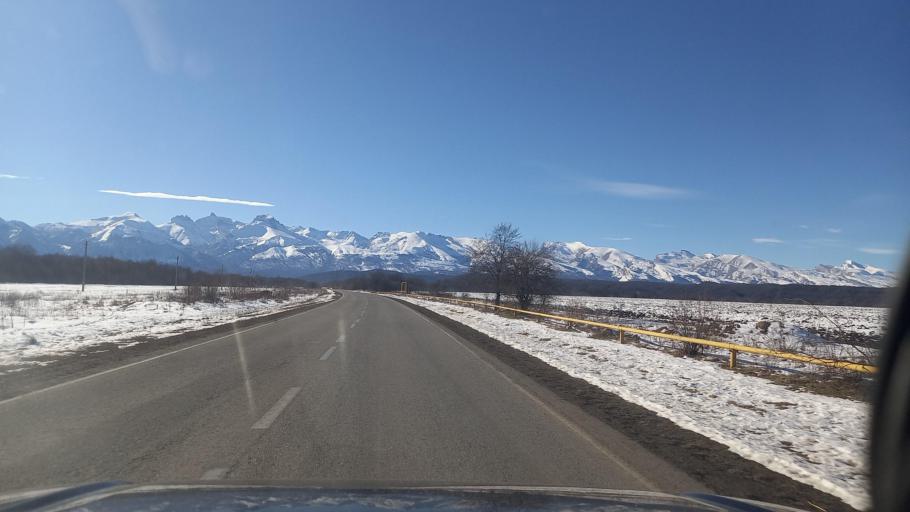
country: RU
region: North Ossetia
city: Chikola
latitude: 43.1698
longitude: 43.8652
